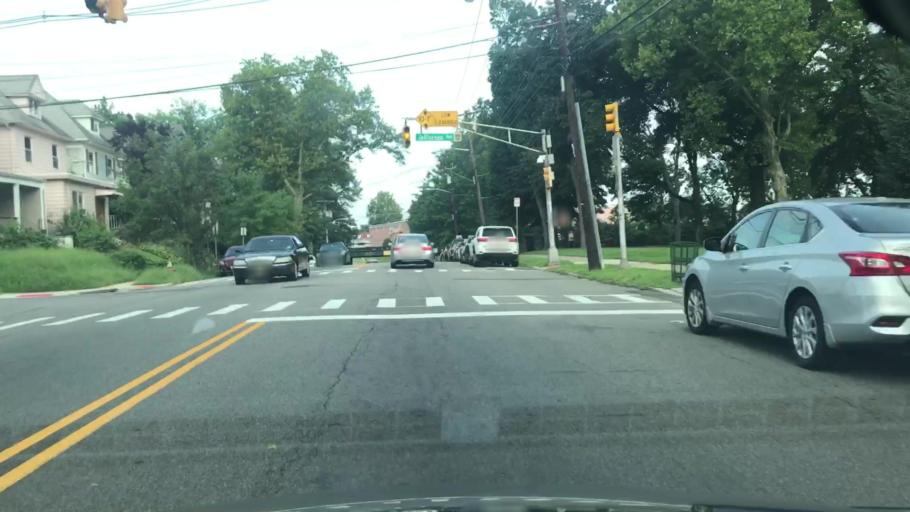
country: US
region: New Jersey
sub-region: Union County
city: Elizabeth
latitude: 40.6803
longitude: -74.2040
